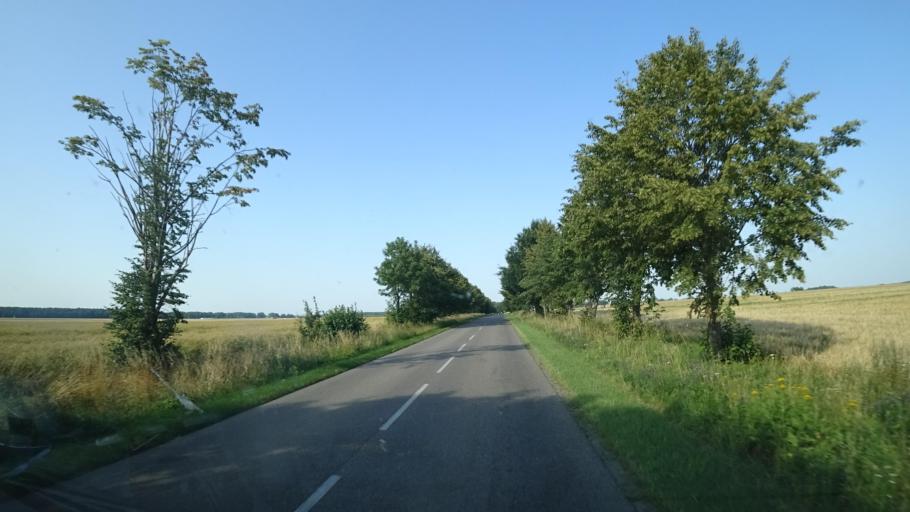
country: PL
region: Pomeranian Voivodeship
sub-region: Powiat czluchowski
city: Przechlewo
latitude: 53.8161
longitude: 17.3618
